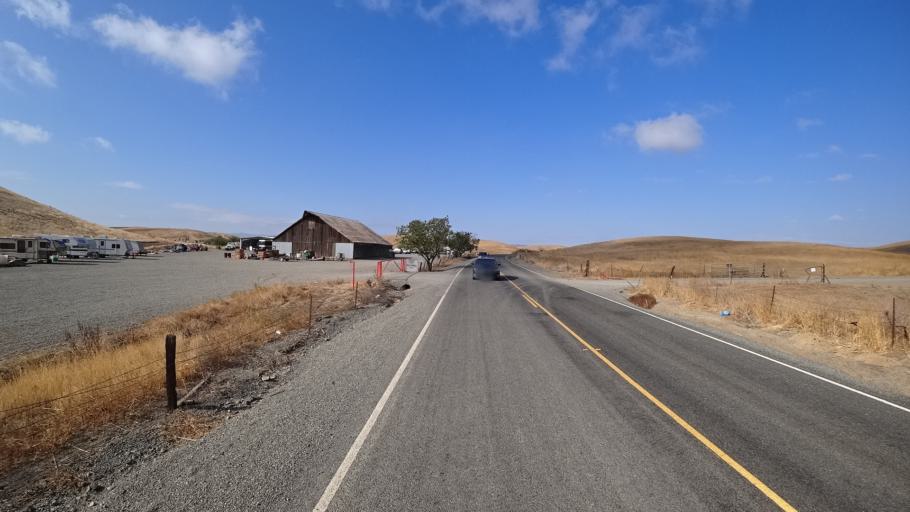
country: US
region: California
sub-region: Yolo County
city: Esparto
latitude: 38.7762
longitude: -121.9557
